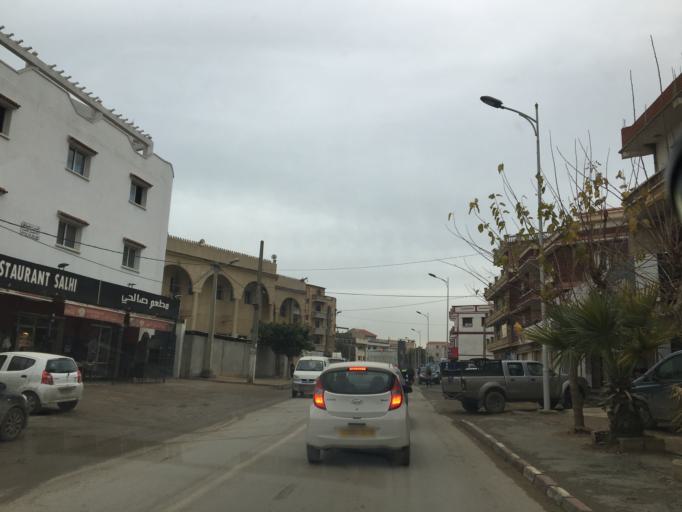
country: DZ
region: Alger
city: Ain Taya
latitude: 36.7787
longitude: 3.2498
